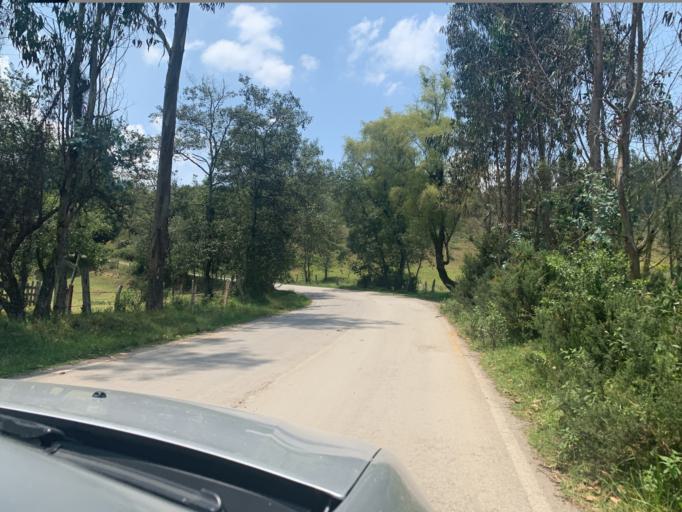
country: CO
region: Boyaca
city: Chiquinquira
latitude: 5.5762
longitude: -73.7465
